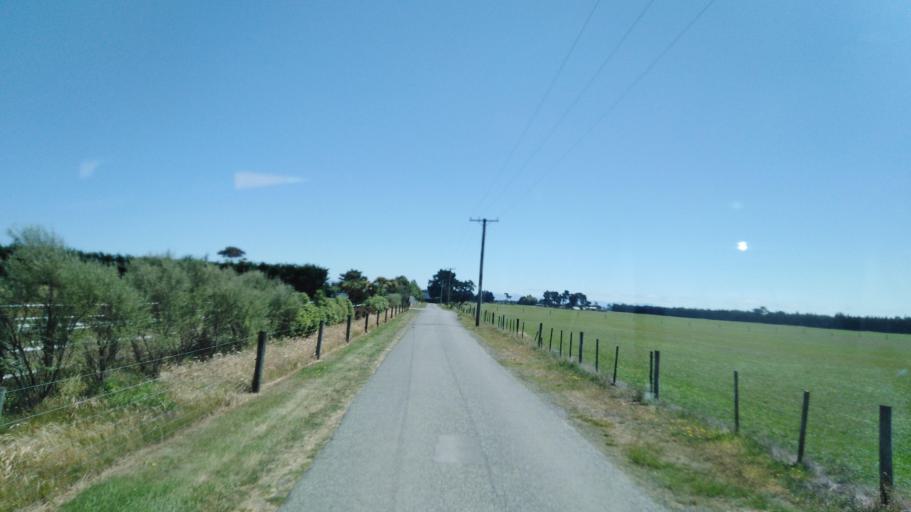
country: NZ
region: Canterbury
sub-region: Selwyn District
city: Rolleston
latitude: -43.5644
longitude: 172.4386
